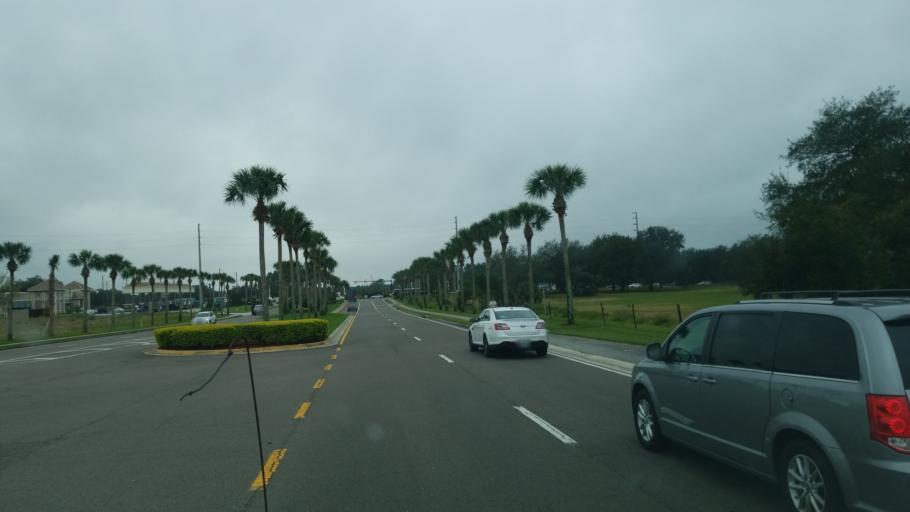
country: US
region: Florida
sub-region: Polk County
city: Loughman
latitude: 28.2577
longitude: -81.6241
